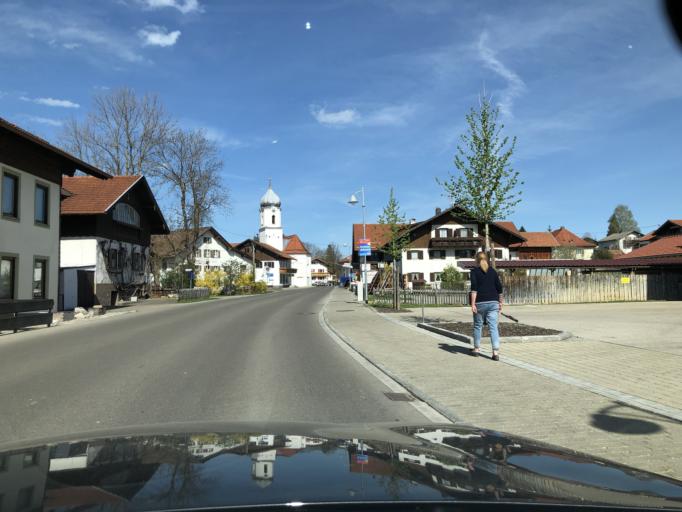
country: DE
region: Bavaria
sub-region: Swabia
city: Hopferau
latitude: 47.6117
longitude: 10.6356
